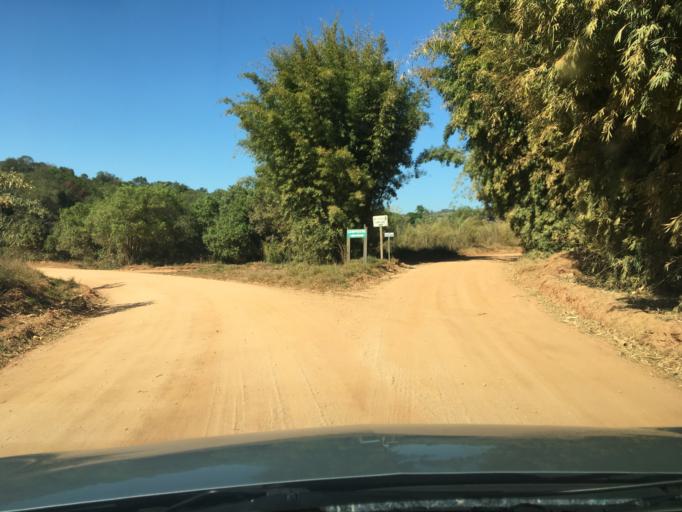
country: BR
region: Minas Gerais
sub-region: Campestre
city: Campestre
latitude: -21.5633
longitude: -46.1979
